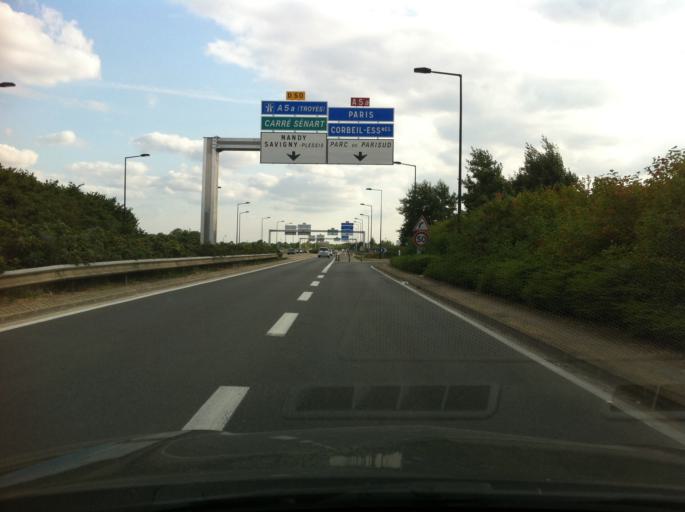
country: FR
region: Ile-de-France
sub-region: Departement de Seine-et-Marne
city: Lieusaint
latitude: 48.6203
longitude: 2.5560
